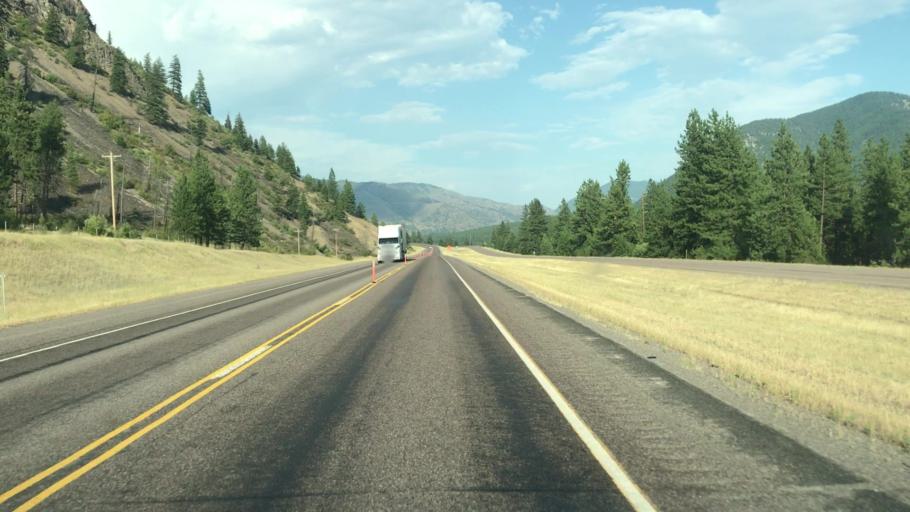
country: US
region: Montana
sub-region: Mineral County
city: Superior
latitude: 47.0124
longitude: -114.7088
